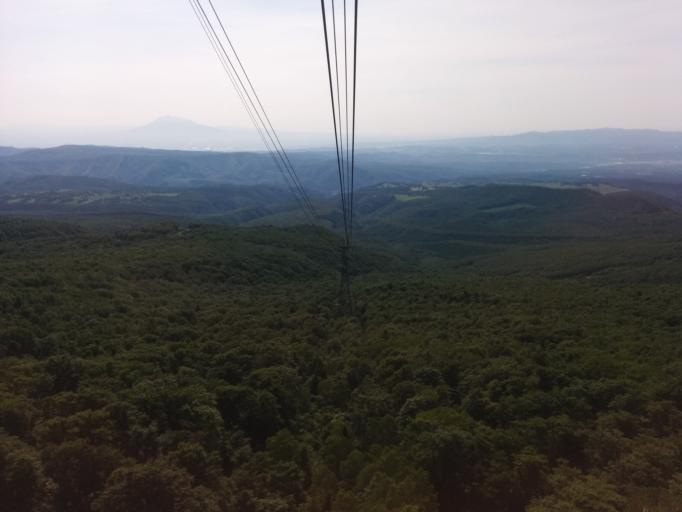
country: JP
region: Aomori
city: Aomori Shi
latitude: 40.6774
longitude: 140.8506
